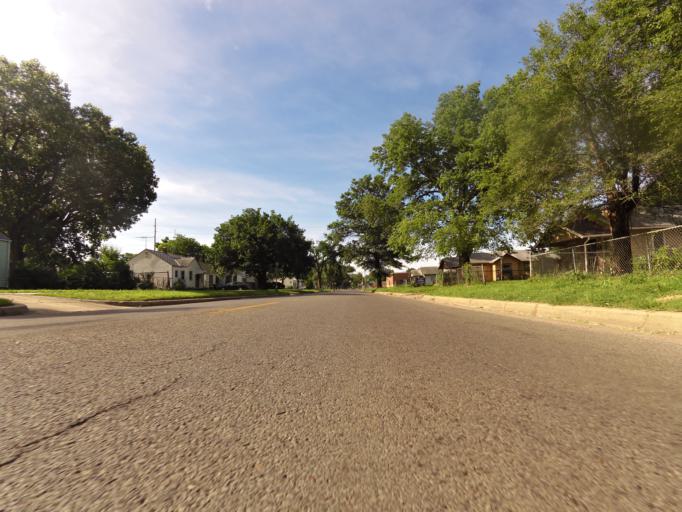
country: US
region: Kansas
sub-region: Sedgwick County
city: Wichita
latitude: 37.7055
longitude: -97.3082
